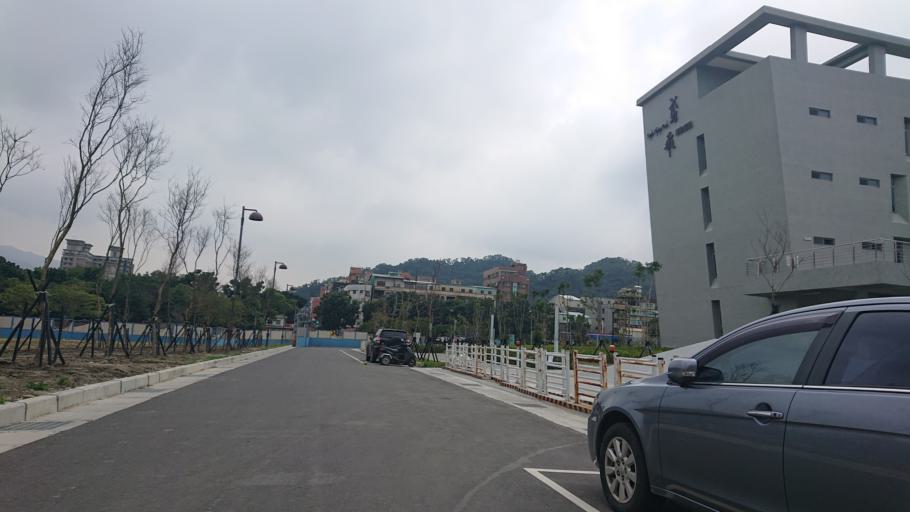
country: TW
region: Taiwan
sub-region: Taoyuan
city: Taoyuan
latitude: 24.9405
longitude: 121.3670
